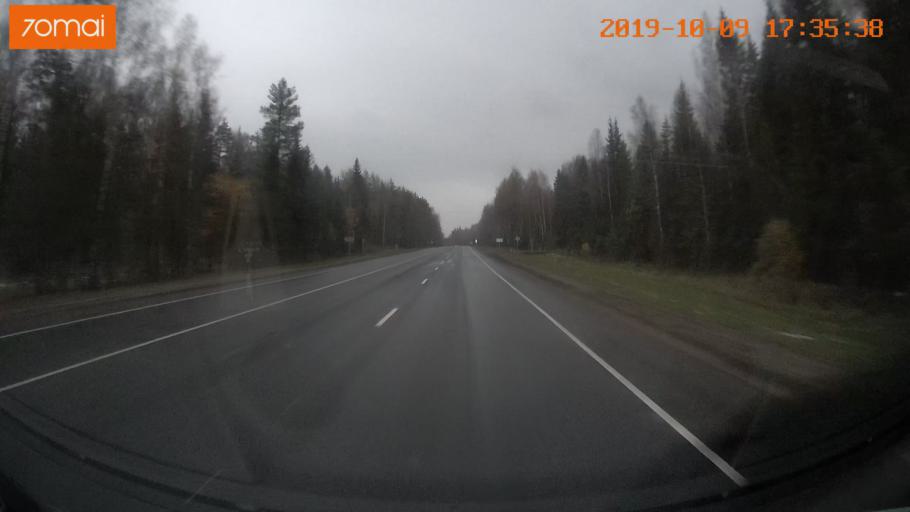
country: RU
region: Ivanovo
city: Bogorodskoye
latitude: 57.0904
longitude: 41.0007
